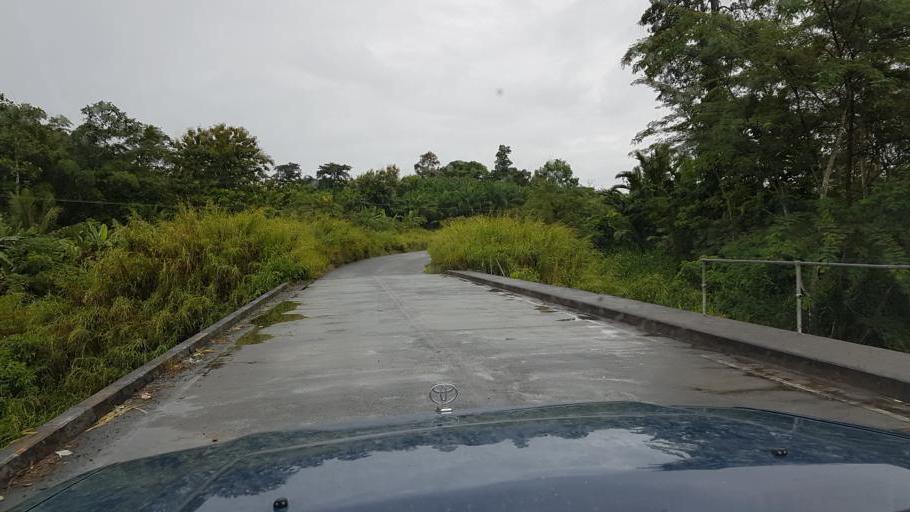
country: PG
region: Northern Province
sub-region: Sohe
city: Popondetta
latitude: -8.8025
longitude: 148.2312
